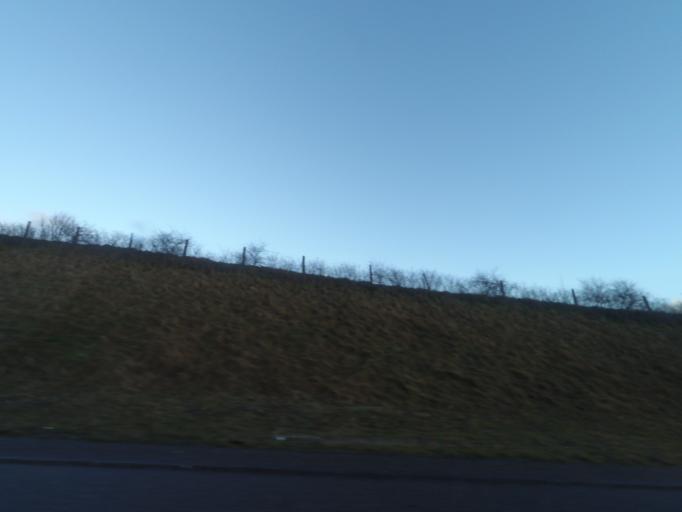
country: DK
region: Central Jutland
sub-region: Herning Kommune
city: Lind
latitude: 56.1042
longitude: 9.0082
